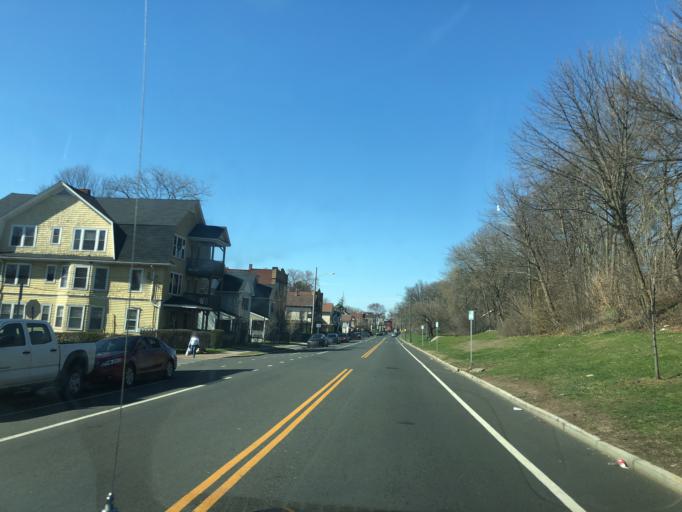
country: US
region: Connecticut
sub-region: Hartford County
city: Hartford
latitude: 41.7468
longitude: -72.6940
